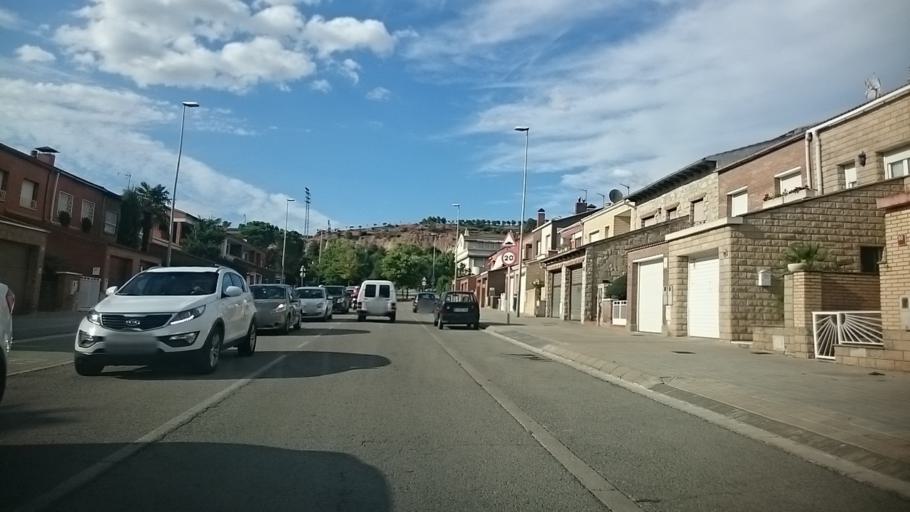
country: ES
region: Catalonia
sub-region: Provincia de Barcelona
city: Igualada
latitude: 41.5929
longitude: 1.6217
